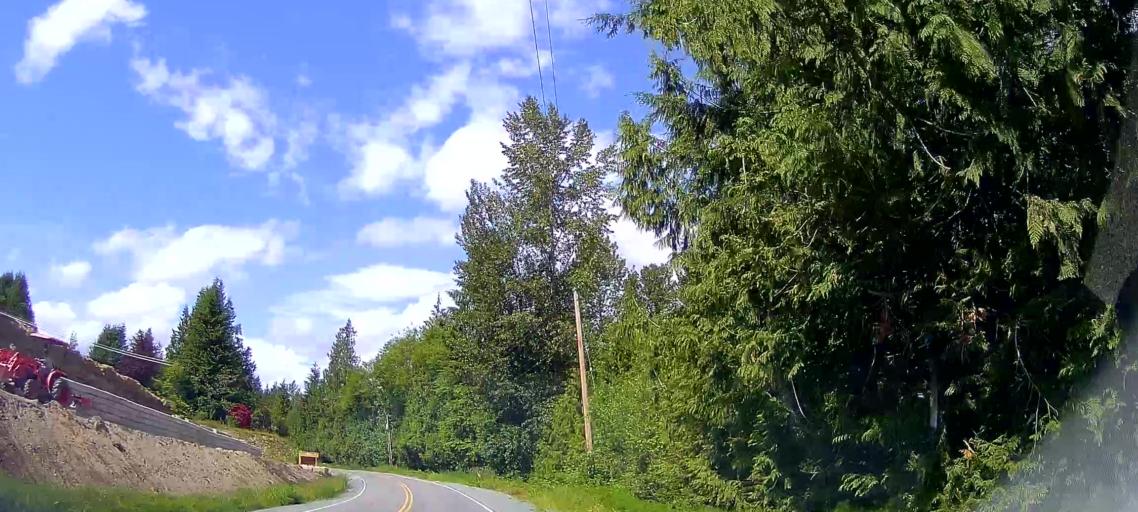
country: US
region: Washington
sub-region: Skagit County
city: Sedro-Woolley
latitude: 48.5542
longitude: -122.2117
